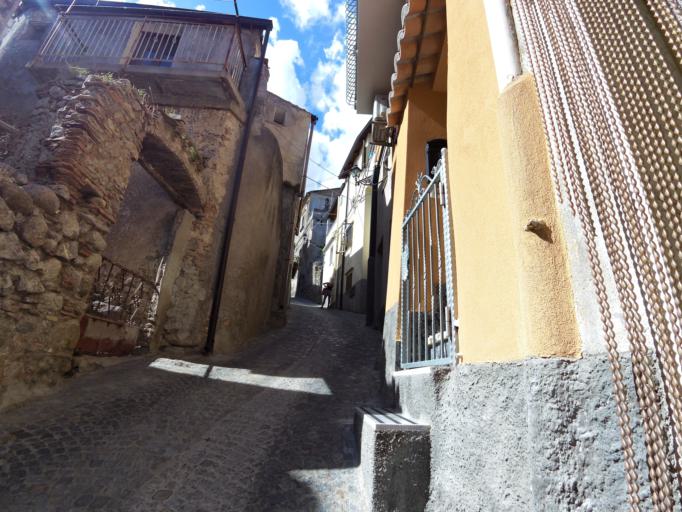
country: IT
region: Calabria
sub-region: Provincia di Reggio Calabria
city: Riace
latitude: 38.4173
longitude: 16.4831
